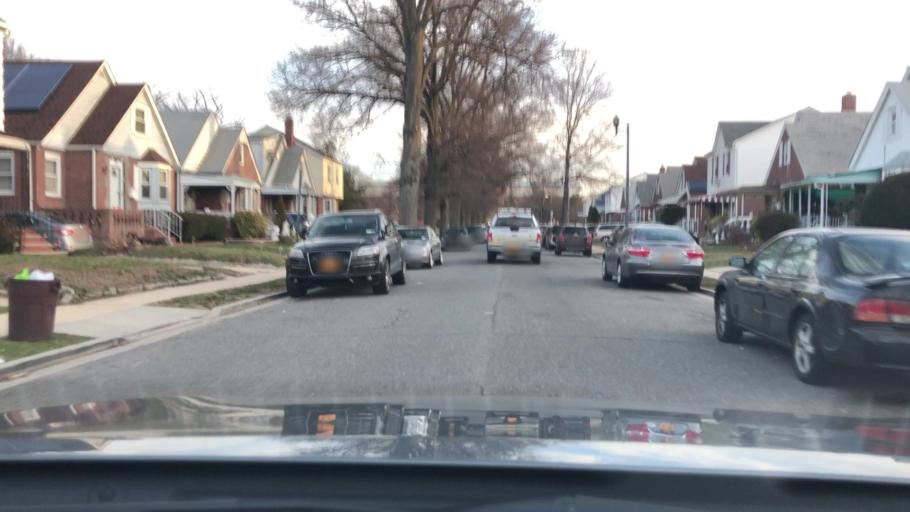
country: US
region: New York
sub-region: Nassau County
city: Bellerose Terrace
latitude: 40.7079
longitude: -73.7240
